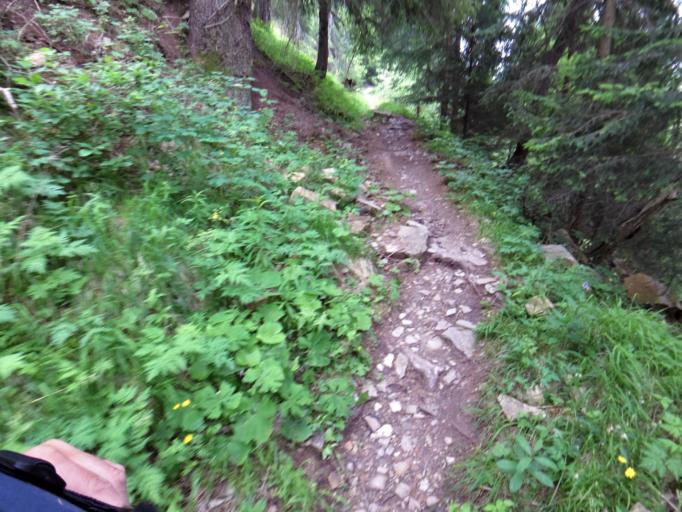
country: IT
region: Trentino-Alto Adige
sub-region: Bolzano
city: Siusi
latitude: 46.5448
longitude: 11.5837
